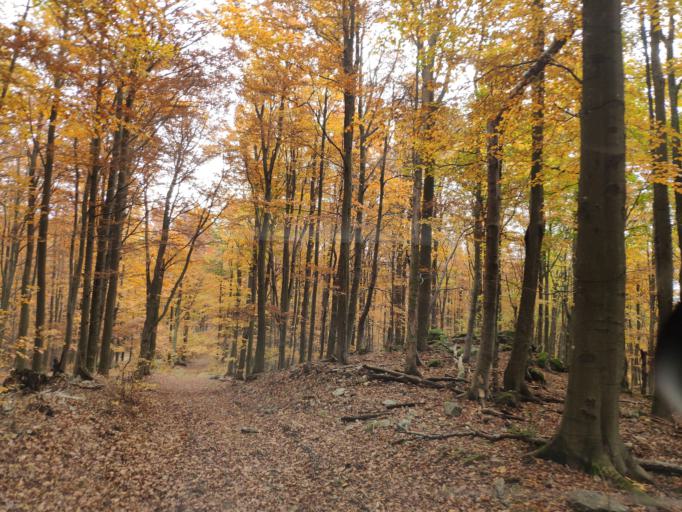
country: SK
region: Kosicky
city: Medzev
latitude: 48.7335
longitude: 21.0076
